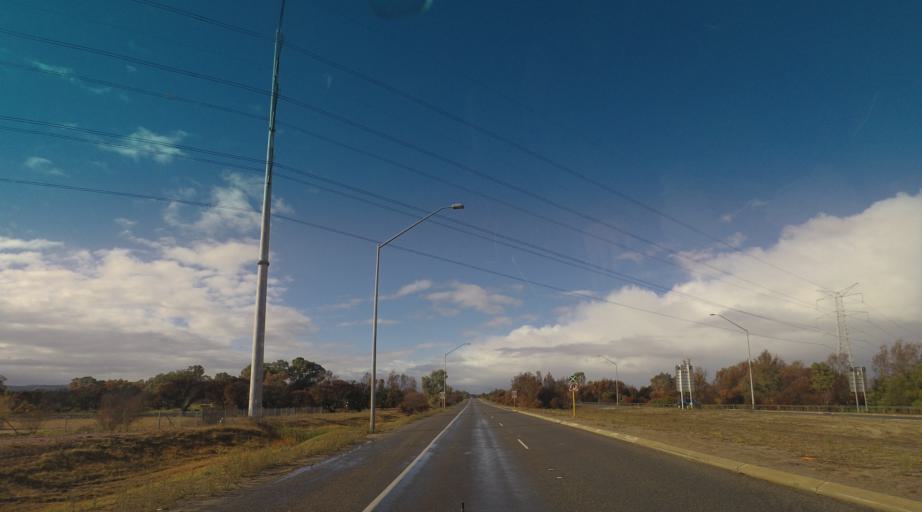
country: AU
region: Western Australia
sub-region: Armadale
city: Seville Grove
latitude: -32.1482
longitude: 115.9572
